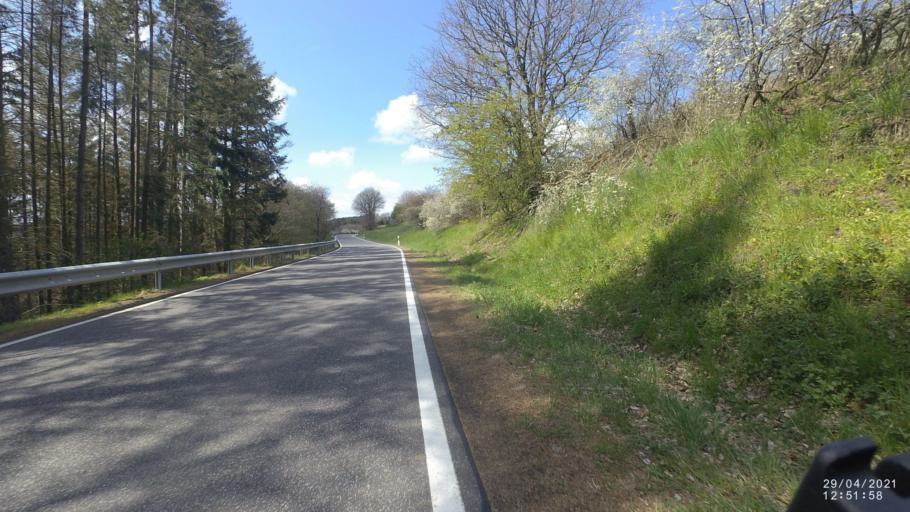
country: DE
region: Rheinland-Pfalz
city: Kirchwald
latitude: 50.3696
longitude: 7.1360
